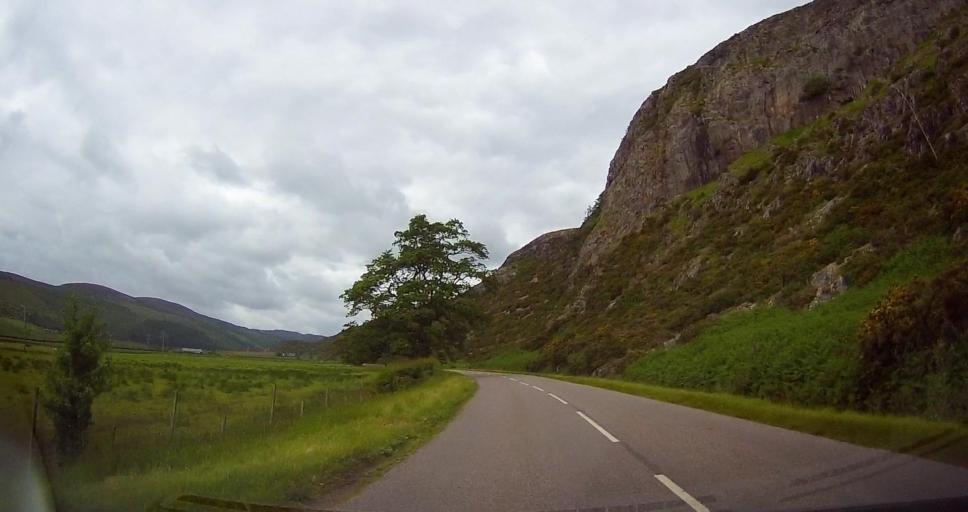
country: GB
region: Scotland
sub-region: Highland
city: Dornoch
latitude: 57.9813
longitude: -4.1168
